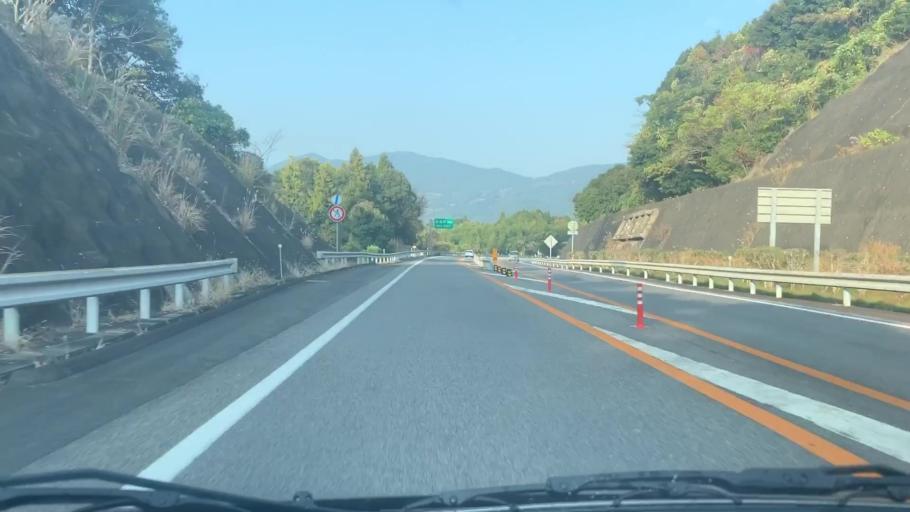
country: JP
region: Saga Prefecture
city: Imaricho-ko
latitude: 33.1659
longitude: 129.8593
